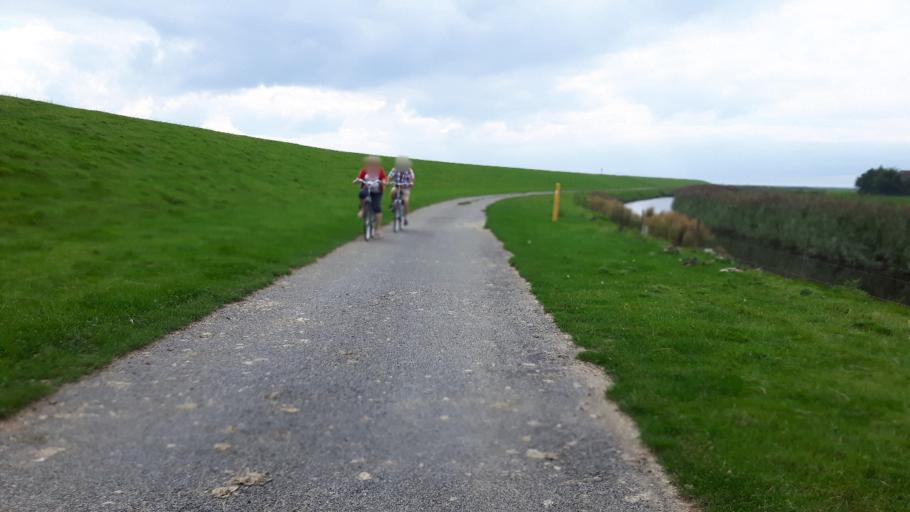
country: NL
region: Friesland
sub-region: Gemeente Ameland
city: Nes
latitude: 53.4434
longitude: 5.8337
